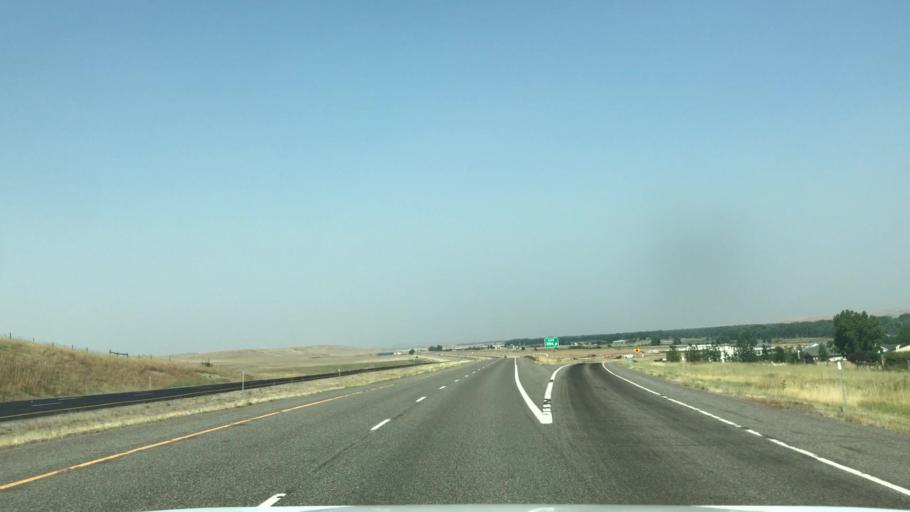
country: US
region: Montana
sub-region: Cascade County
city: Sun Prairie
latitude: 47.2769
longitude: -111.7044
